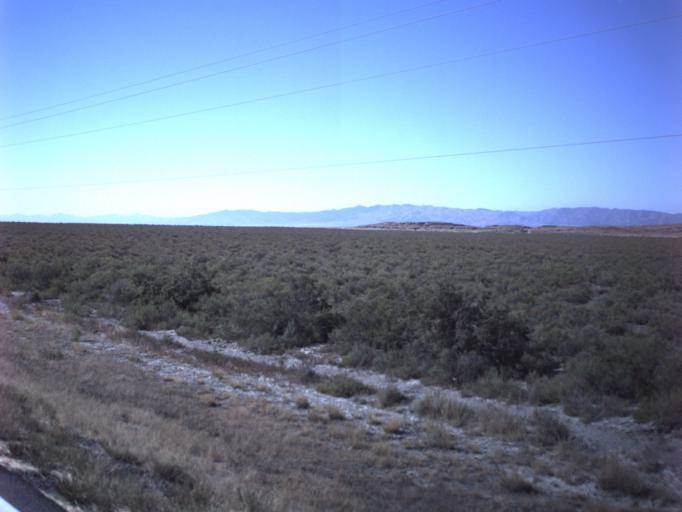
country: US
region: Utah
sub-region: Tooele County
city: Grantsville
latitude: 40.7134
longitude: -112.6622
